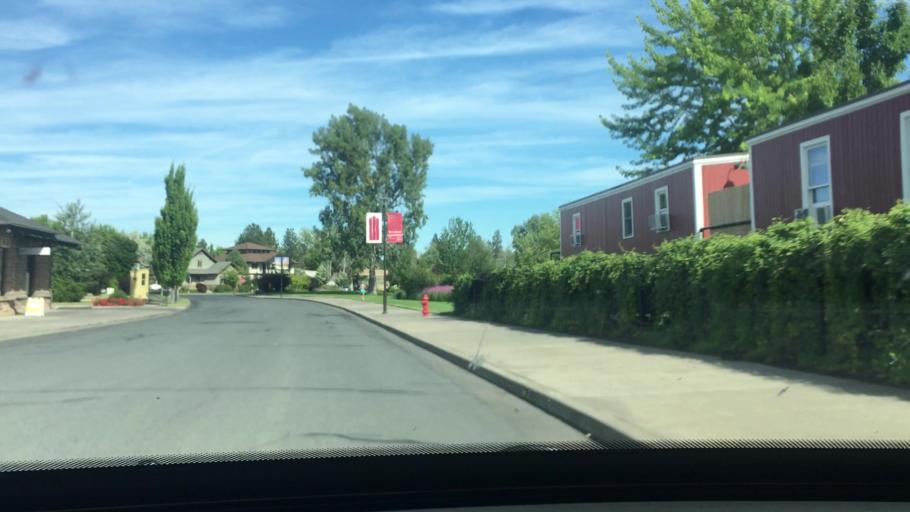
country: US
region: Oregon
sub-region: Deschutes County
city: Bend
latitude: 44.0476
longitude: -121.3193
